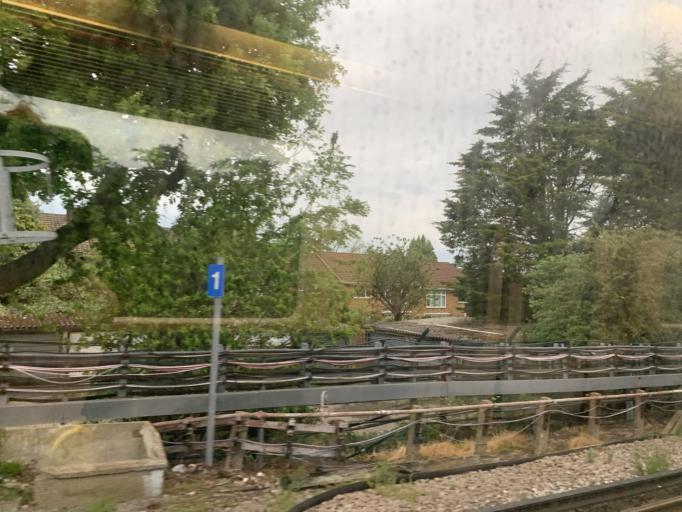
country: GB
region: England
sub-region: Essex
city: Buckhurst Hill
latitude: 51.6173
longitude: 0.0448
